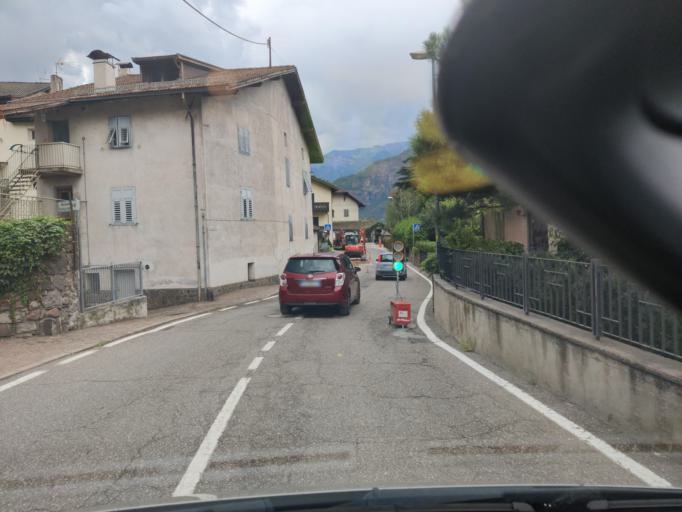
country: IT
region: Trentino-Alto Adige
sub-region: Bolzano
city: Bronzolo
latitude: 46.4068
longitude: 11.3219
